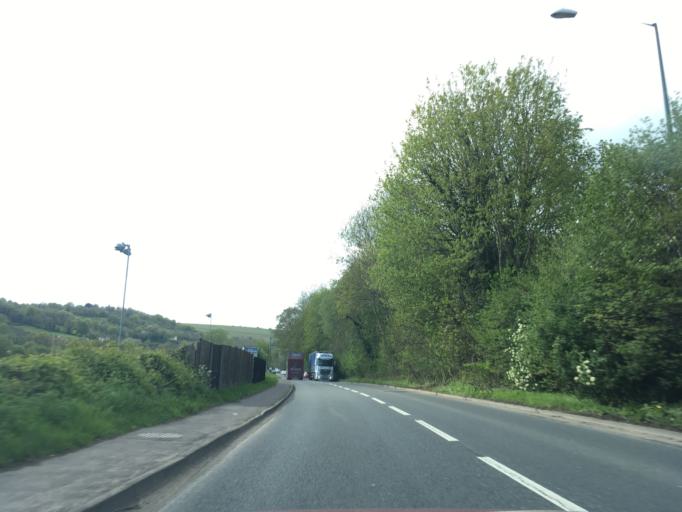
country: GB
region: England
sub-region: Gloucestershire
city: Brimscombe
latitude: 51.7216
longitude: -2.1944
